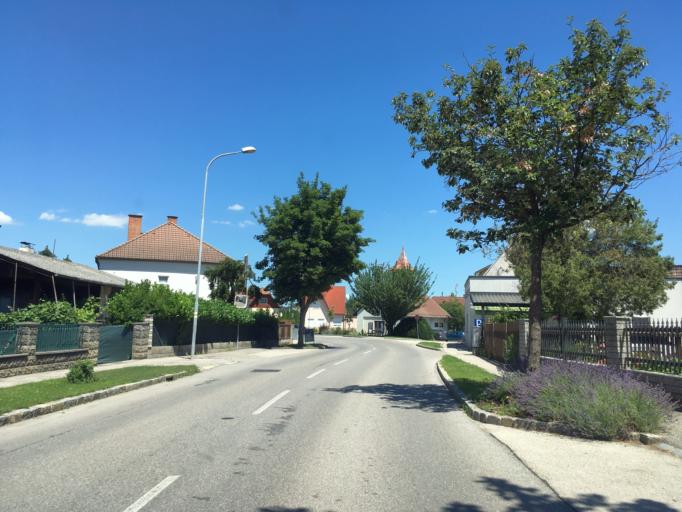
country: AT
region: Lower Austria
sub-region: Politischer Bezirk Wiener Neustadt
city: Bad Erlach
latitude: 47.7249
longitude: 16.2123
